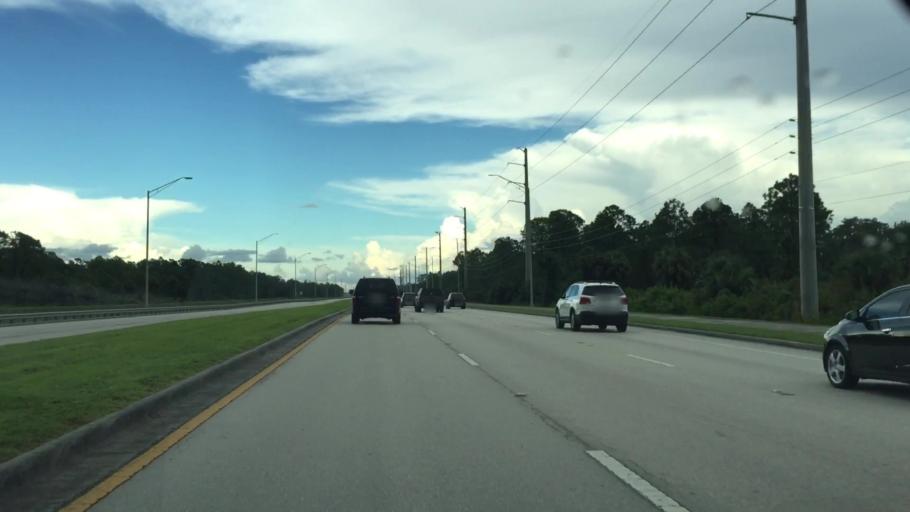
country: US
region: Florida
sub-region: Collier County
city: Orangetree
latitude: 26.2757
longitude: -81.6189
